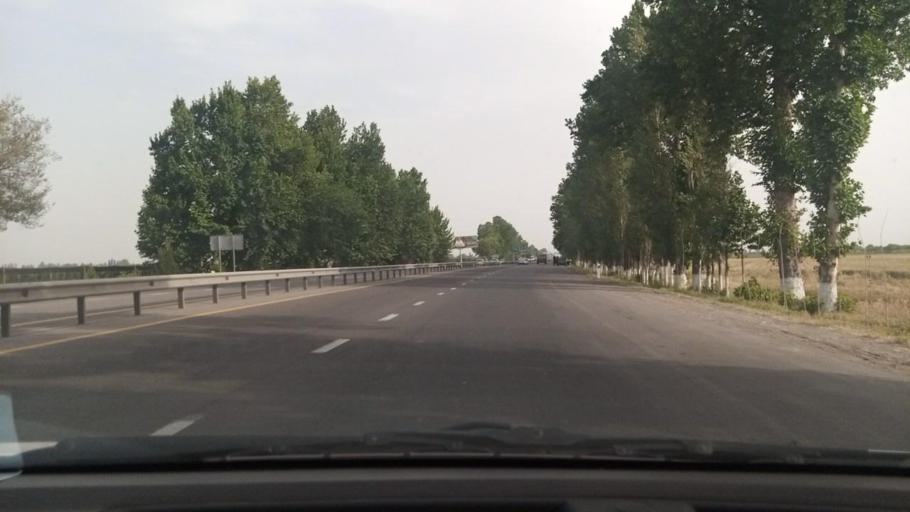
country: UZ
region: Toshkent Shahri
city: Bektemir
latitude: 41.2381
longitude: 69.4020
